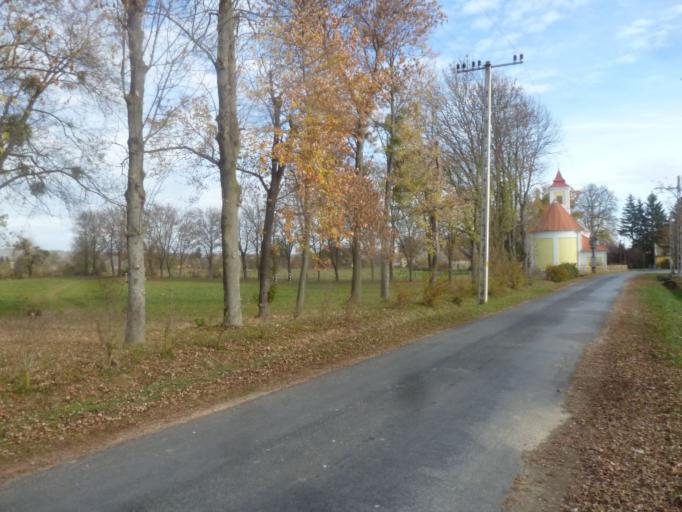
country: HU
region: Zala
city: Pacsa
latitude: 46.6259
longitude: 17.0586
